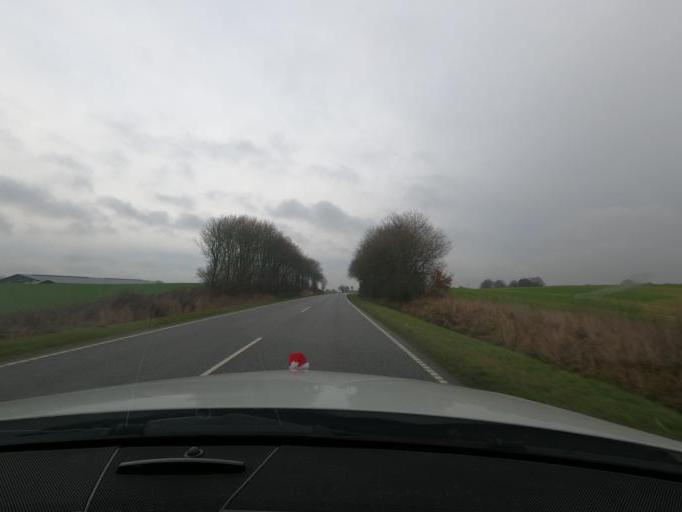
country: DK
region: South Denmark
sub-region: Haderslev Kommune
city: Haderslev
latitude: 55.1974
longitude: 9.4251
